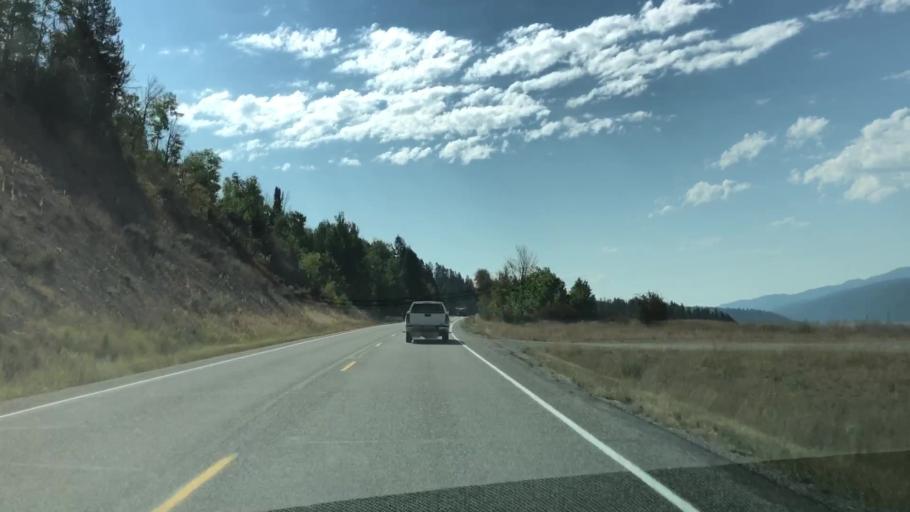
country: US
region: Idaho
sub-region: Teton County
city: Victor
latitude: 43.2929
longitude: -111.1250
